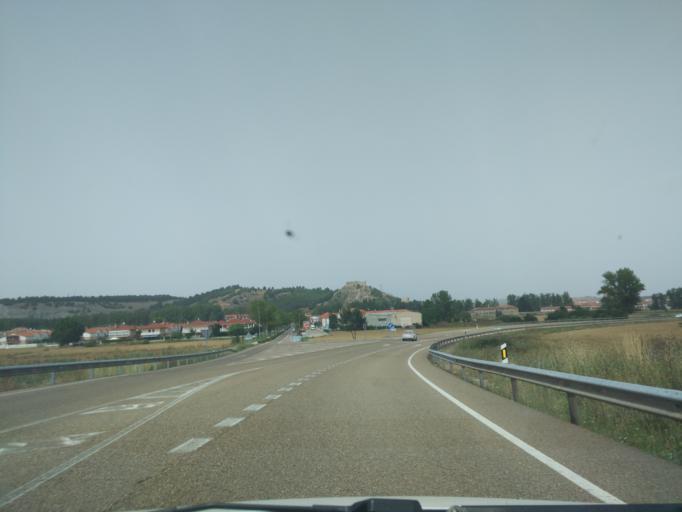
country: ES
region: Castille and Leon
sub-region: Provincia de Palencia
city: Aguilar de Campoo
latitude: 42.7852
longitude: -4.2665
